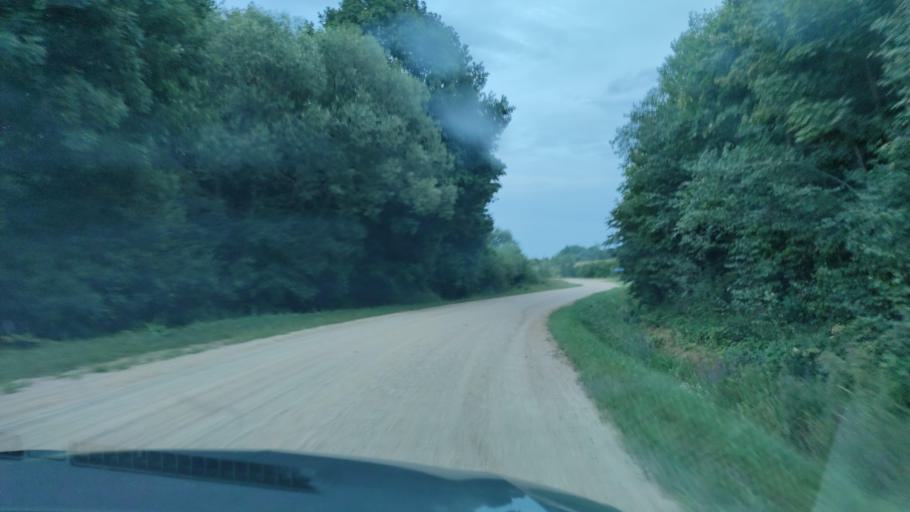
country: BY
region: Vitebsk
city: Mosar
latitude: 55.0737
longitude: 27.2087
